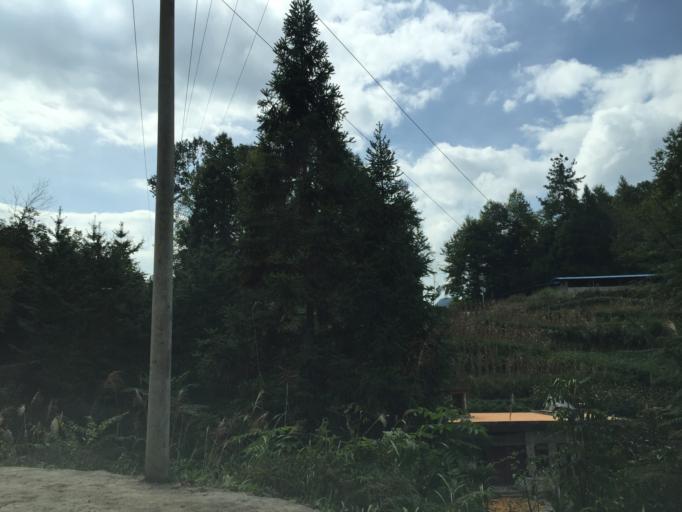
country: CN
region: Guizhou Sheng
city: Quankou
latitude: 28.5356
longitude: 108.1167
